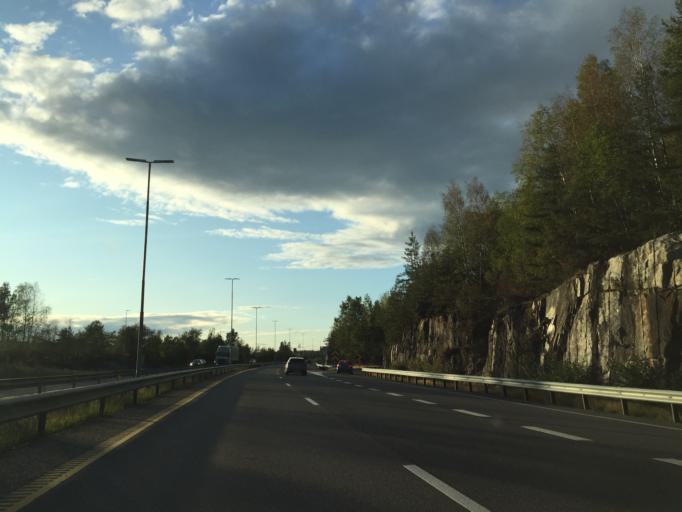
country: NO
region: Akershus
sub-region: Lorenskog
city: Kjenn
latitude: 59.9309
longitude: 10.9464
